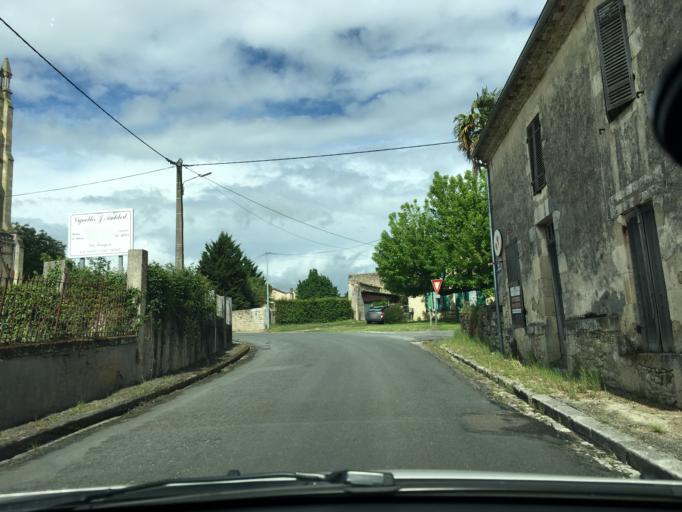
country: FR
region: Aquitaine
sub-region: Departement de la Gironde
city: Vertheuil
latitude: 45.3220
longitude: -0.8192
